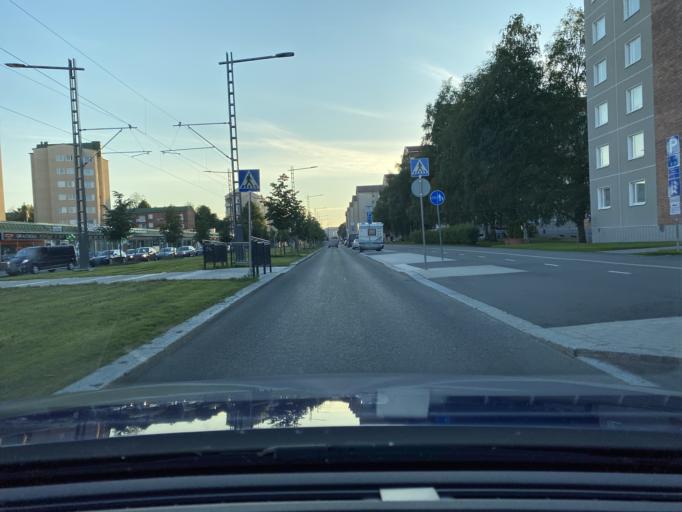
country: FI
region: Pirkanmaa
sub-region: Tampere
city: Tampere
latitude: 61.4971
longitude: 23.8001
